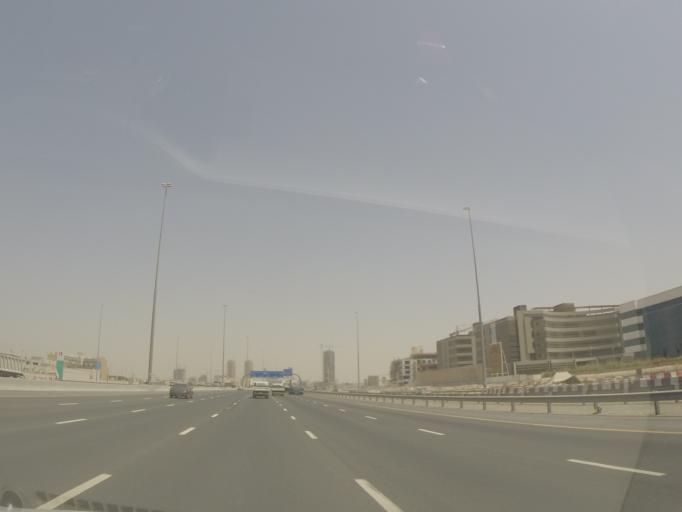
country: AE
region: Dubai
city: Dubai
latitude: 25.0384
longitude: 55.1837
